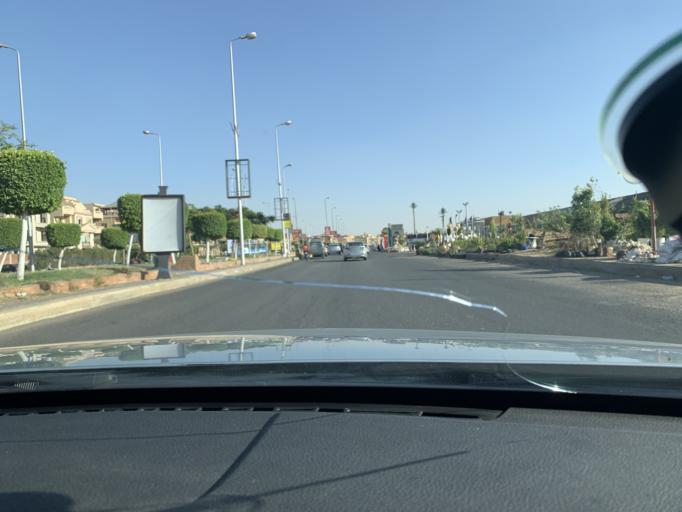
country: EG
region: Muhafazat al Qalyubiyah
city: Al Khankah
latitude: 30.0509
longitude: 31.4420
